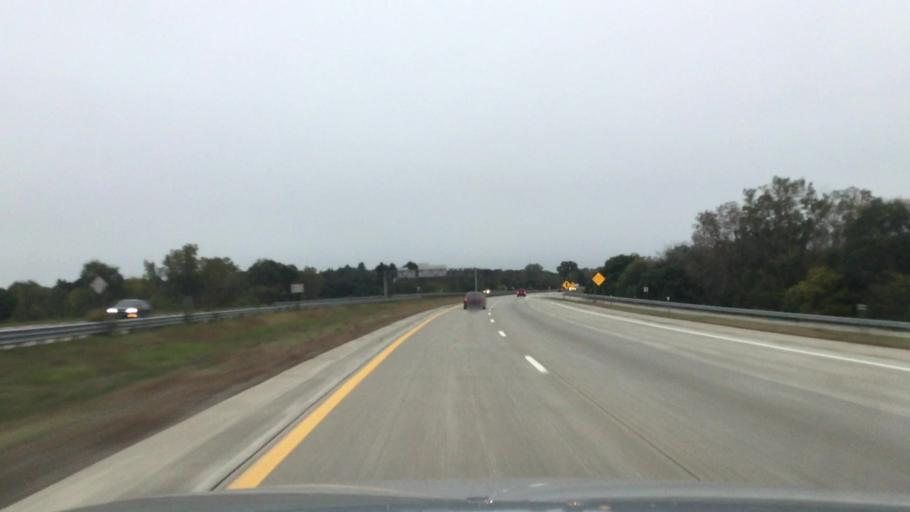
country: US
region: Michigan
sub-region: Genesee County
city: Swartz Creek
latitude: 42.9721
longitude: -83.7670
